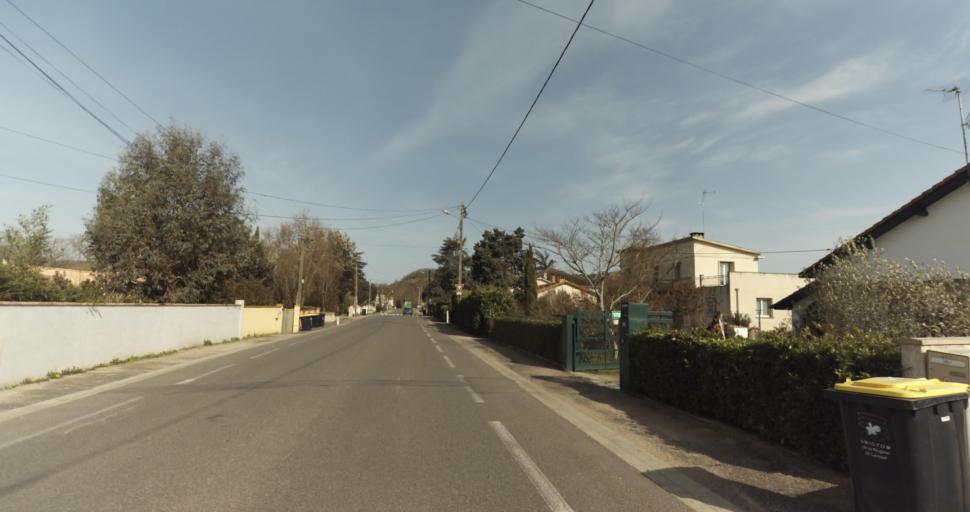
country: FR
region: Midi-Pyrenees
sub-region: Departement du Tarn
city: Saint-Sulpice-la-Pointe
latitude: 43.7816
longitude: 1.6803
